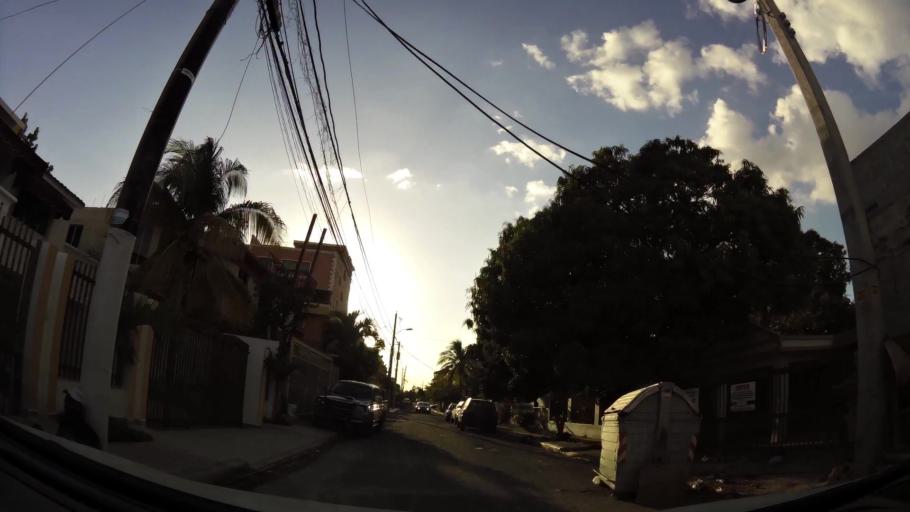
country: DO
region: Santo Domingo
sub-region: Santo Domingo
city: Santo Domingo Este
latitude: 18.4799
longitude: -69.8345
